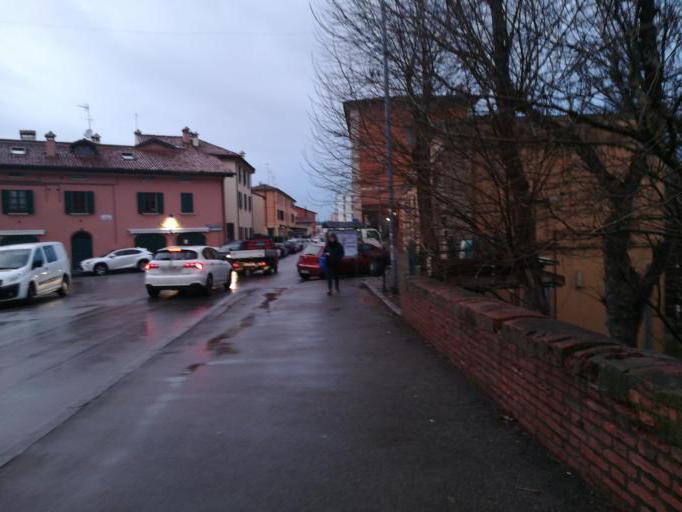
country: IT
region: Emilia-Romagna
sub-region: Provincia di Bologna
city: Progresso
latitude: 44.5491
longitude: 11.3548
